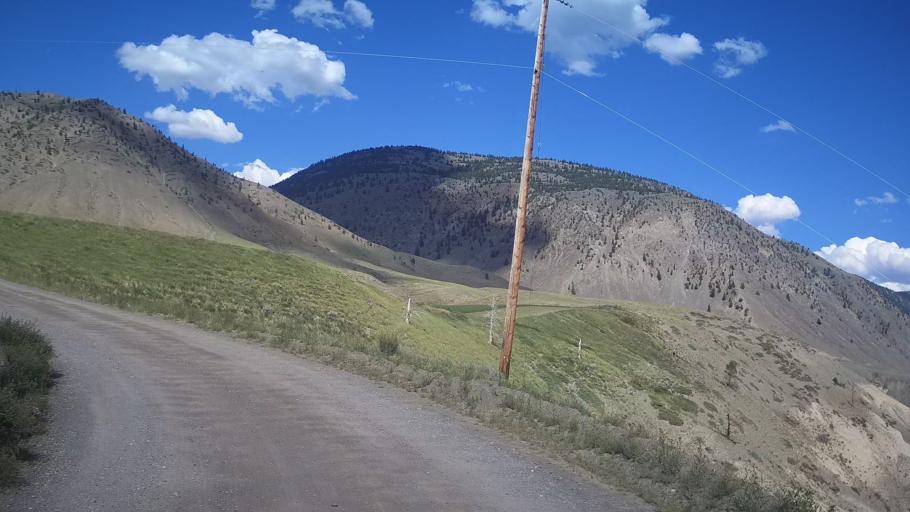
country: CA
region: British Columbia
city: Lillooet
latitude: 51.1834
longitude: -122.1169
